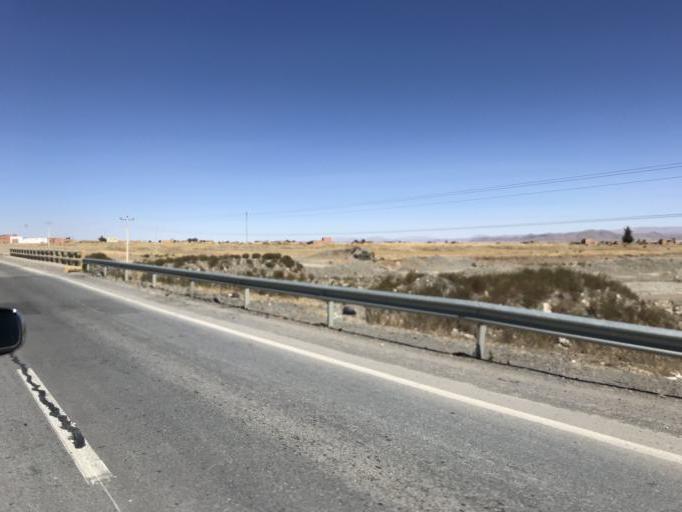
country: BO
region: La Paz
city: Batallas
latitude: -16.3293
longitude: -68.4228
